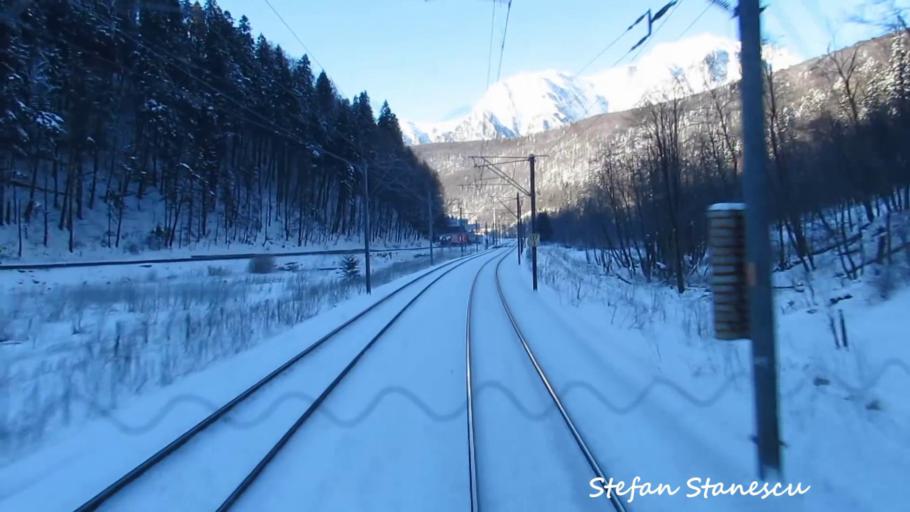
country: RO
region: Prahova
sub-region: Oras Azuga
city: Azuga
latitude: 45.4538
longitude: 25.5639
